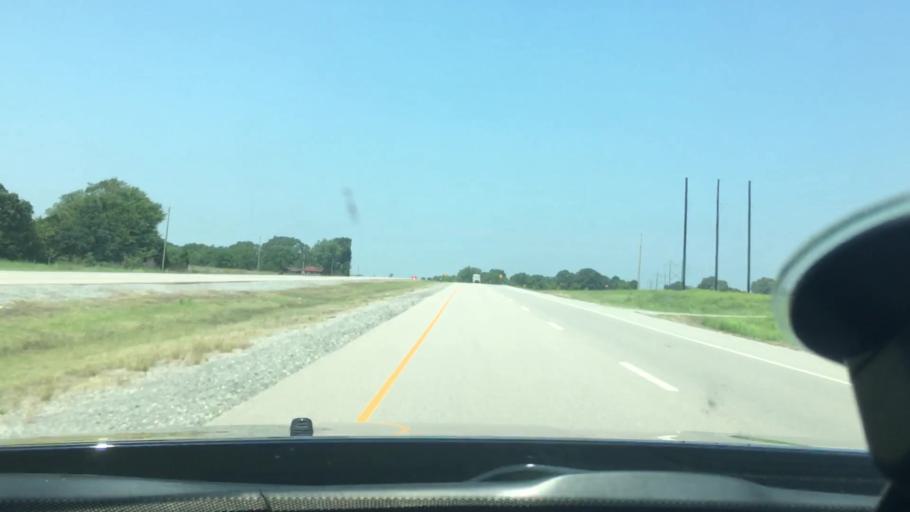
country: US
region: Oklahoma
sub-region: Atoka County
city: Atoka
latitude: 34.3320
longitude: -96.0515
